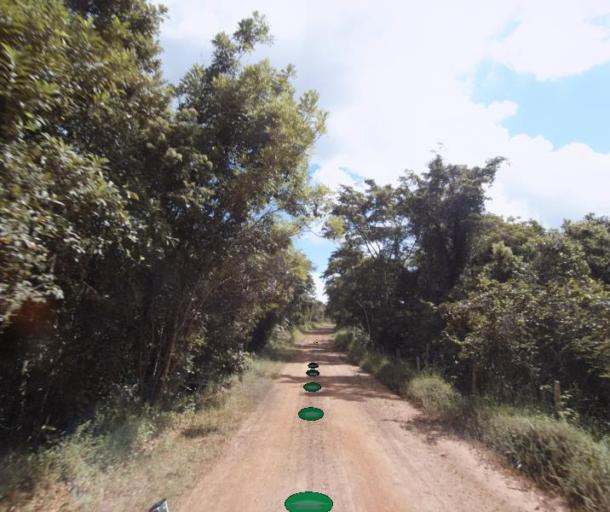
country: BR
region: Goias
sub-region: Pirenopolis
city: Pirenopolis
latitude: -15.7916
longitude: -48.8886
